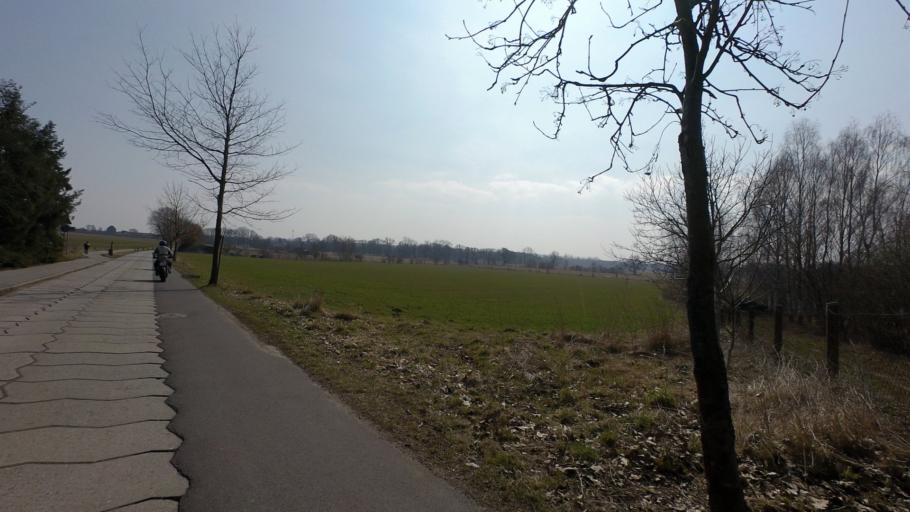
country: DE
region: Brandenburg
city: Gross Kreutz
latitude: 52.4108
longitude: 12.8189
